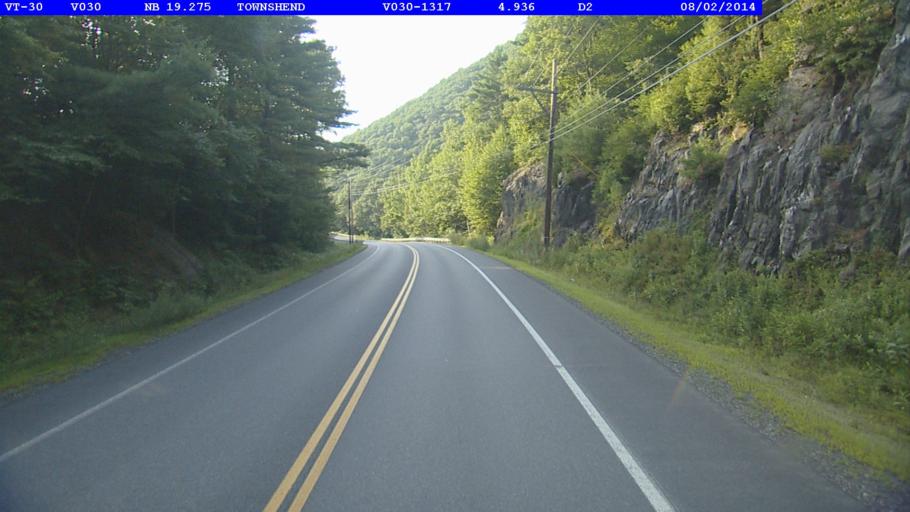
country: US
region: Vermont
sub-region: Windham County
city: Newfane
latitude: 43.0653
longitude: -72.6985
